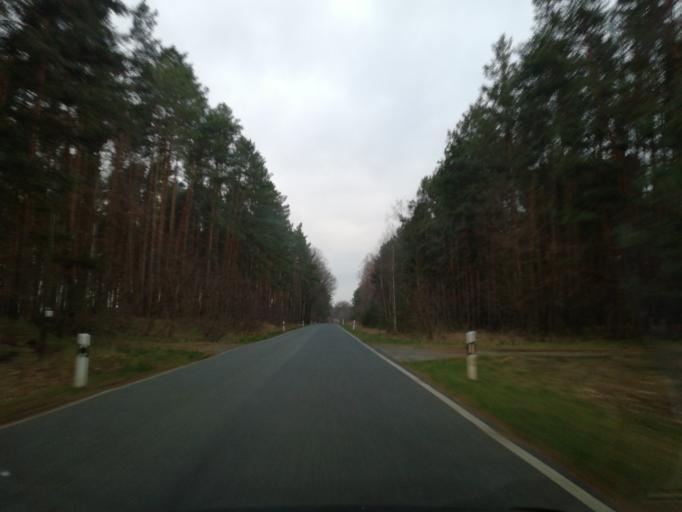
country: DE
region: Brandenburg
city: Vetschau
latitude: 51.7634
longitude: 14.0871
